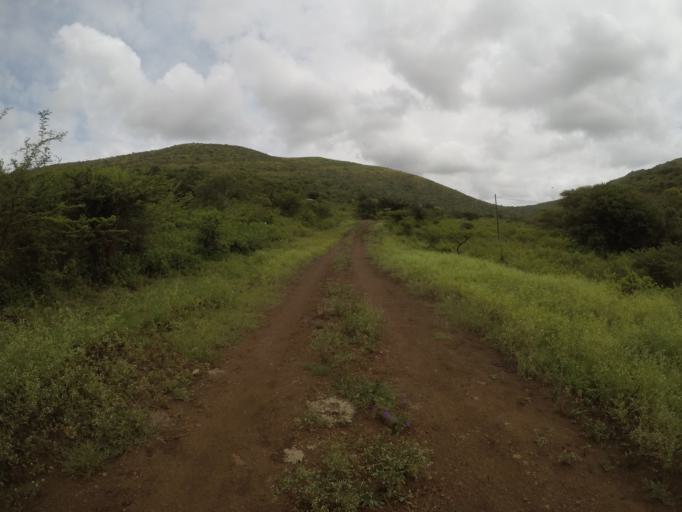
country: ZA
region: KwaZulu-Natal
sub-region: uThungulu District Municipality
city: Empangeni
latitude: -28.5835
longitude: 31.8882
